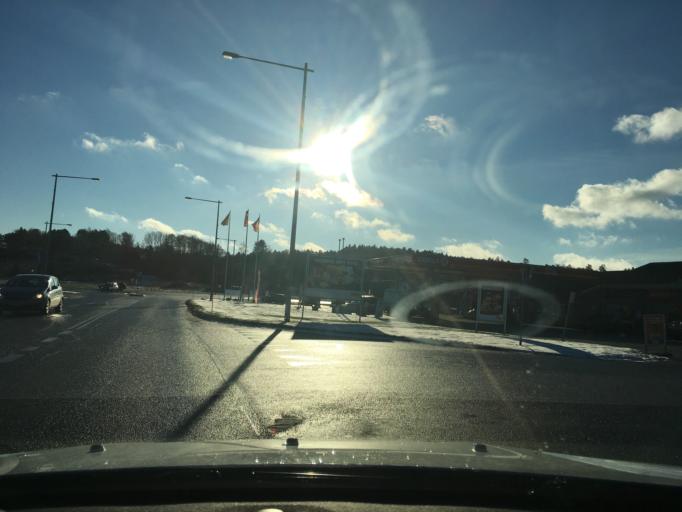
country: SE
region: Vaestra Goetaland
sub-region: Tjorns Kommun
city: Myggenas
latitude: 58.0248
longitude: 11.6566
